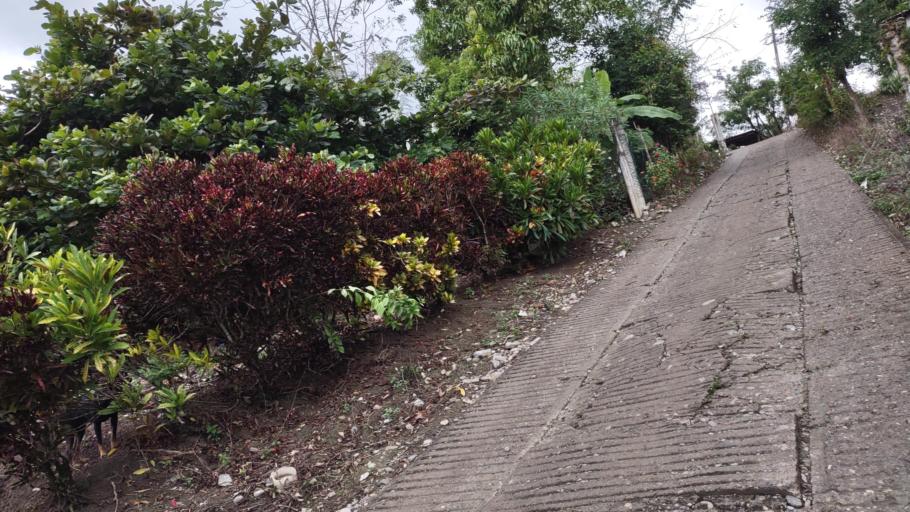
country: MX
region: Puebla
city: Espinal
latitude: 20.2628
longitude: -97.3711
